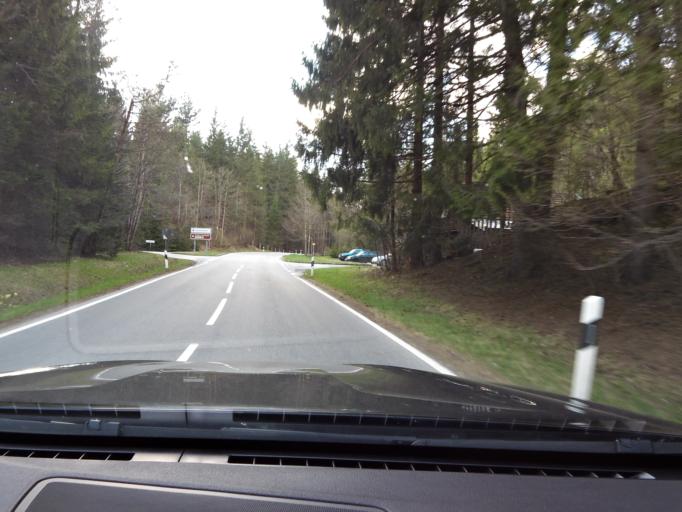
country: DE
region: Bavaria
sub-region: Upper Bavaria
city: Mittenwald
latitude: 47.4562
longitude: 11.2681
